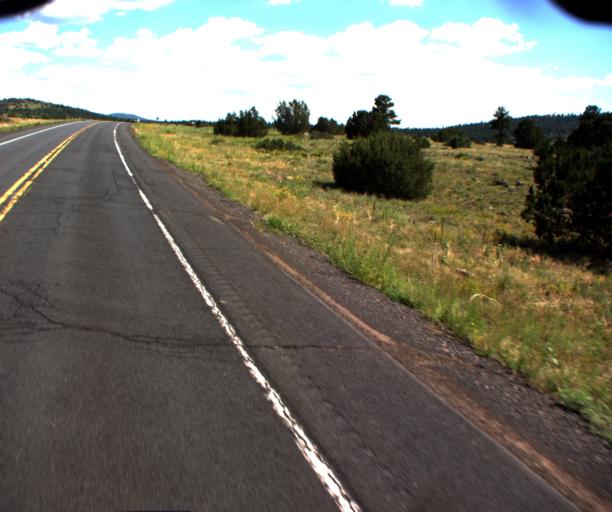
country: US
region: Arizona
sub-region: Coconino County
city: Williams
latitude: 35.3170
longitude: -112.1494
